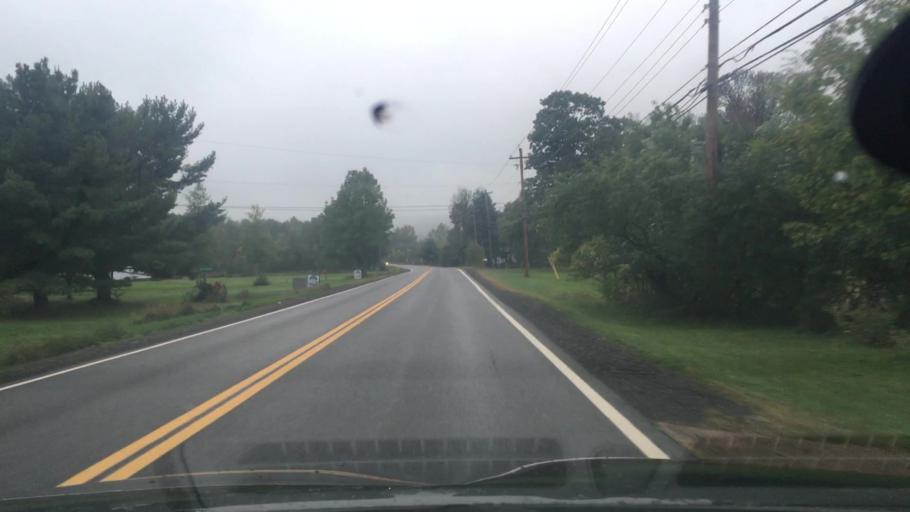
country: CA
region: Nova Scotia
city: Windsor
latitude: 44.9379
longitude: -64.1917
